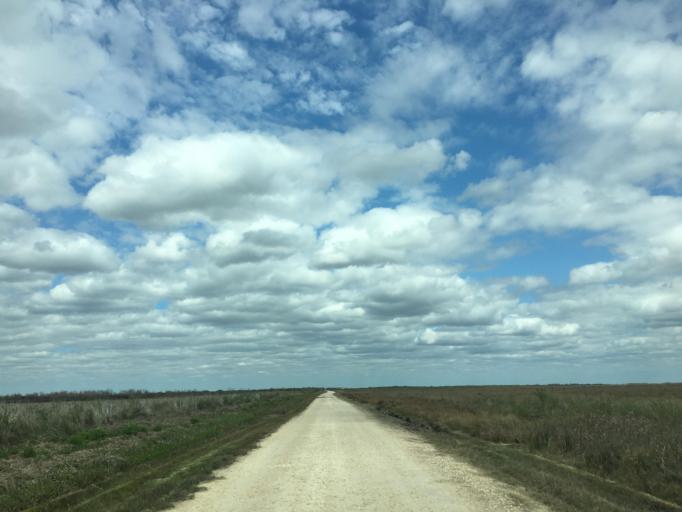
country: US
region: Texas
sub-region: Brazoria County
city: Oyster Creek
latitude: 29.0394
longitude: -95.2680
